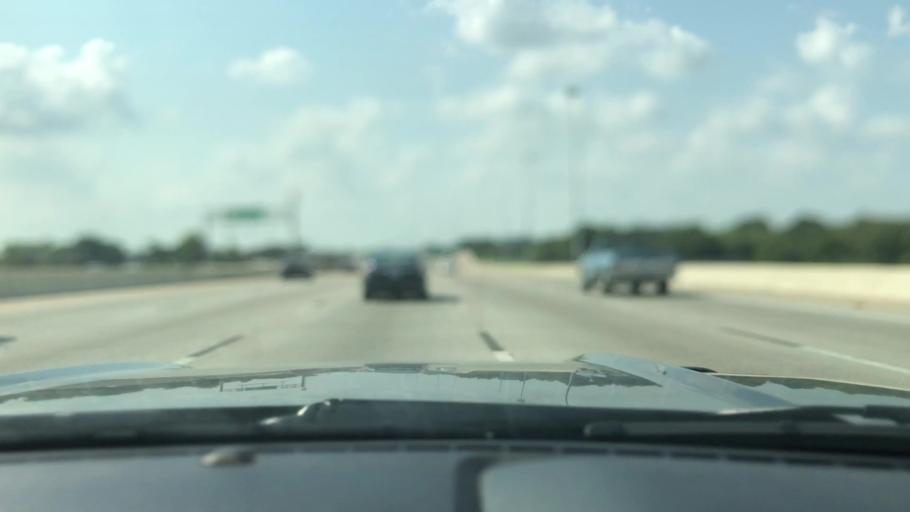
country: US
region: Texas
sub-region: Harris County
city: Aldine
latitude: 29.8594
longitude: -95.3337
